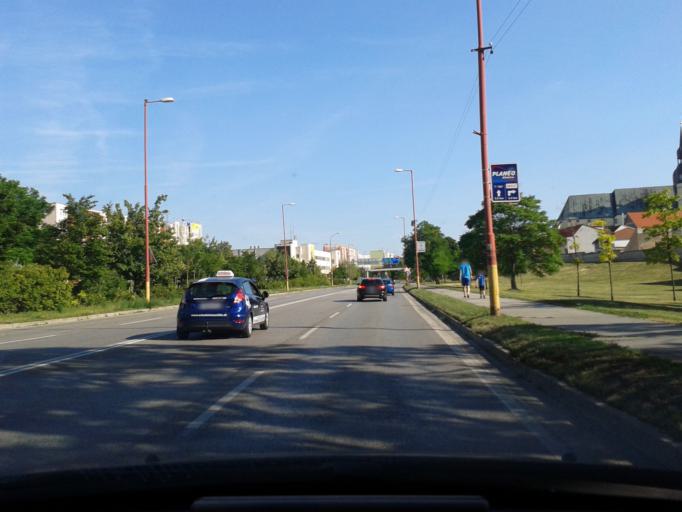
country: SK
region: Trnavsky
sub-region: Okres Trnava
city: Trnava
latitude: 48.3819
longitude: 17.5916
